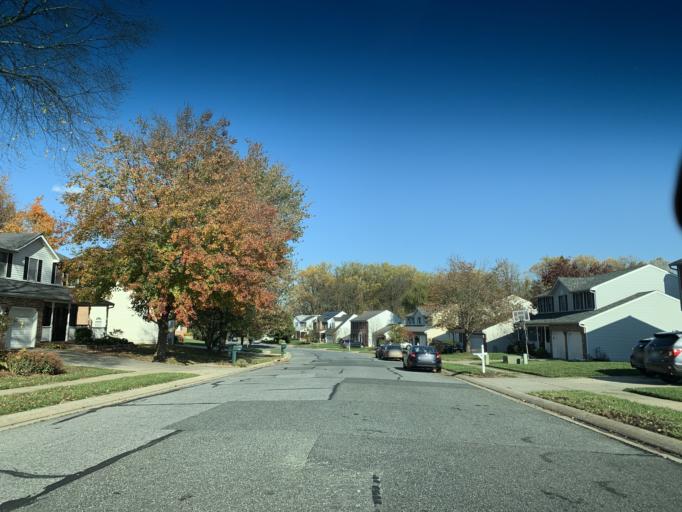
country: US
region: Maryland
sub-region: Harford County
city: Bel Air South
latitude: 39.4973
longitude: -76.3162
